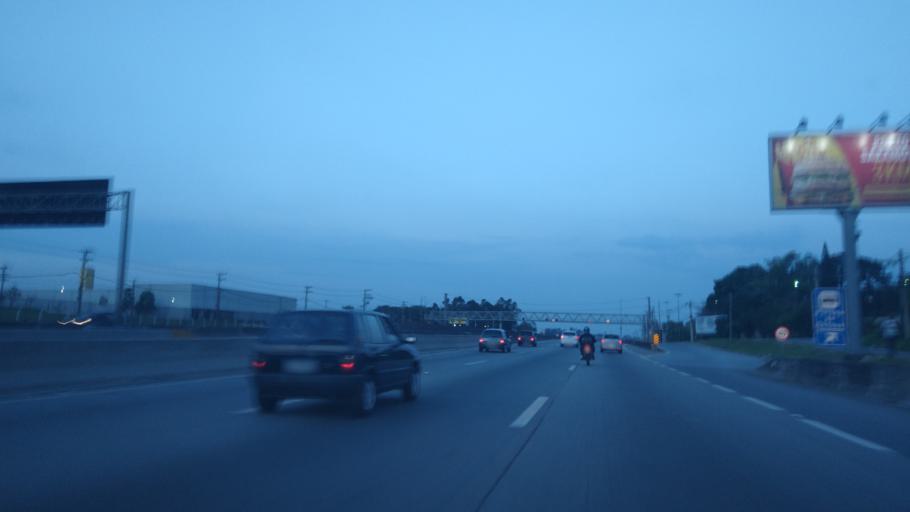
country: BR
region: Sao Paulo
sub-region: Guarulhos
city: Guarulhos
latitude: -23.4450
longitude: -46.4492
